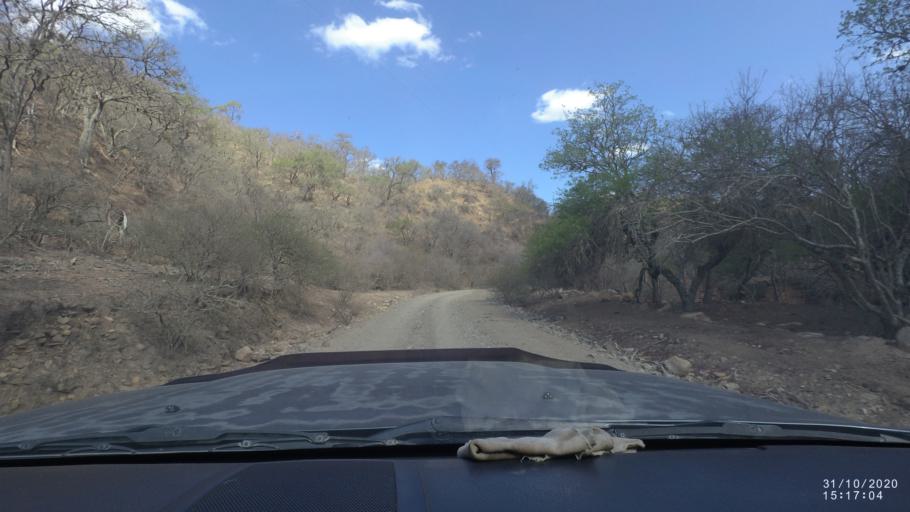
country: BO
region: Cochabamba
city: Aiquile
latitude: -18.3382
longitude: -64.7693
